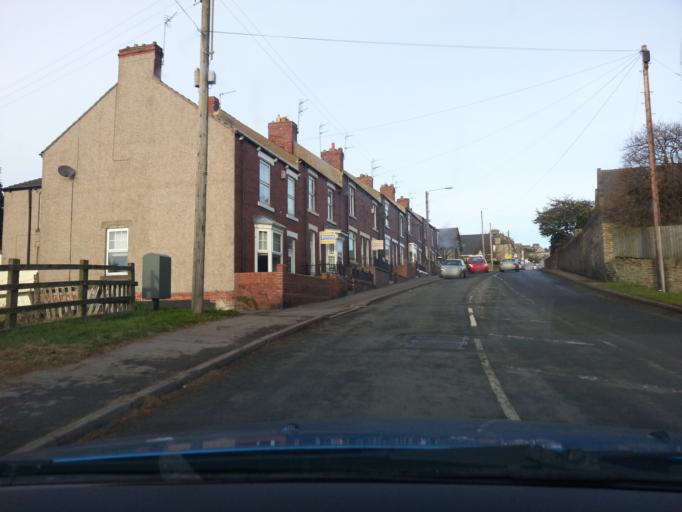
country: GB
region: England
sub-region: County Durham
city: Crook
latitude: 54.7290
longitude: -1.7531
